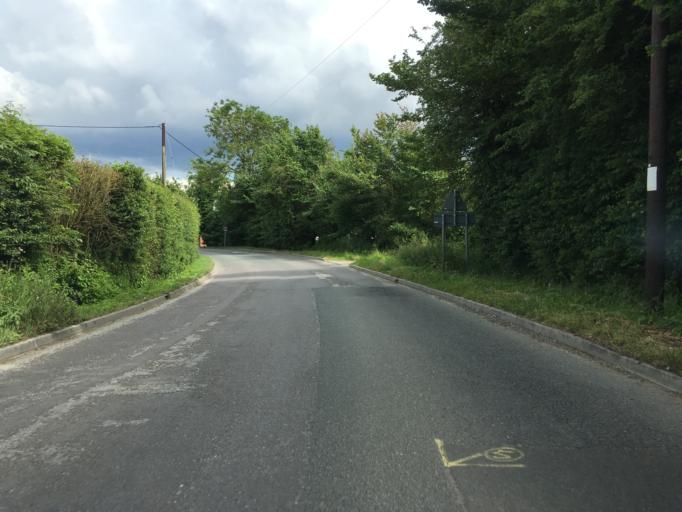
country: GB
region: England
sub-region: Wiltshire
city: Cricklade
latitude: 51.6303
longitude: -1.8780
